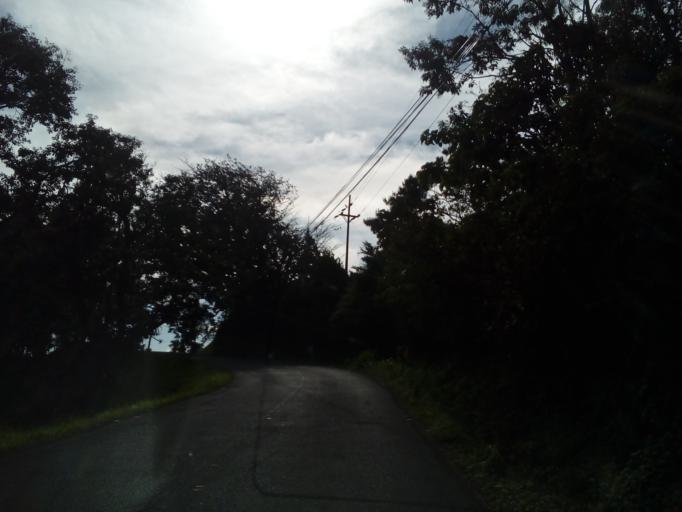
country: CR
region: Guanacaste
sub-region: Canton de Tilaran
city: Tilaran
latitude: 10.5605
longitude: -84.9643
